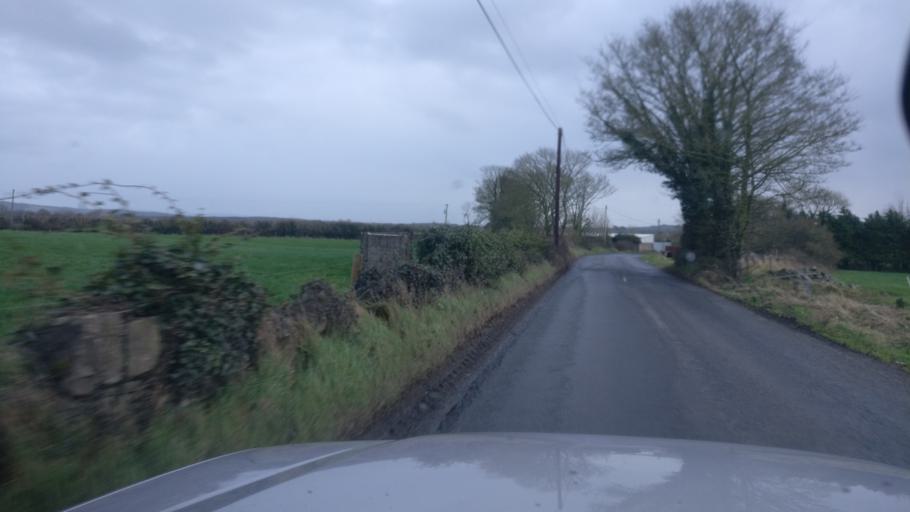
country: IE
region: Munster
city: Nenagh Bridge
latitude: 52.9882
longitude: -8.1153
